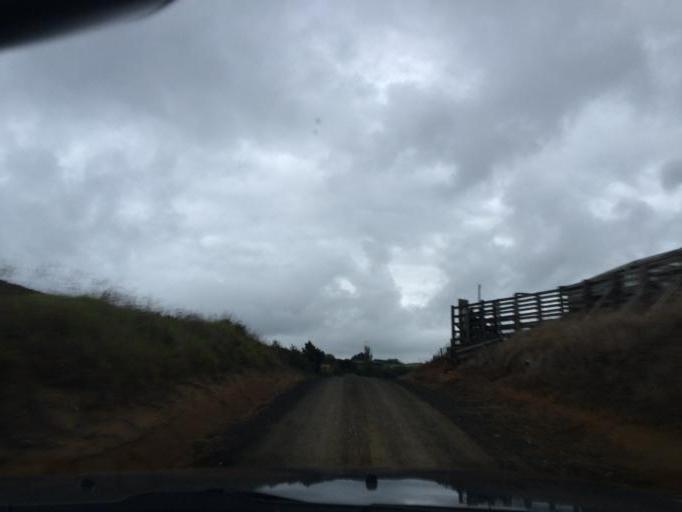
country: NZ
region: Northland
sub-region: Whangarei
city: Maungatapere
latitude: -35.8119
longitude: 174.0604
